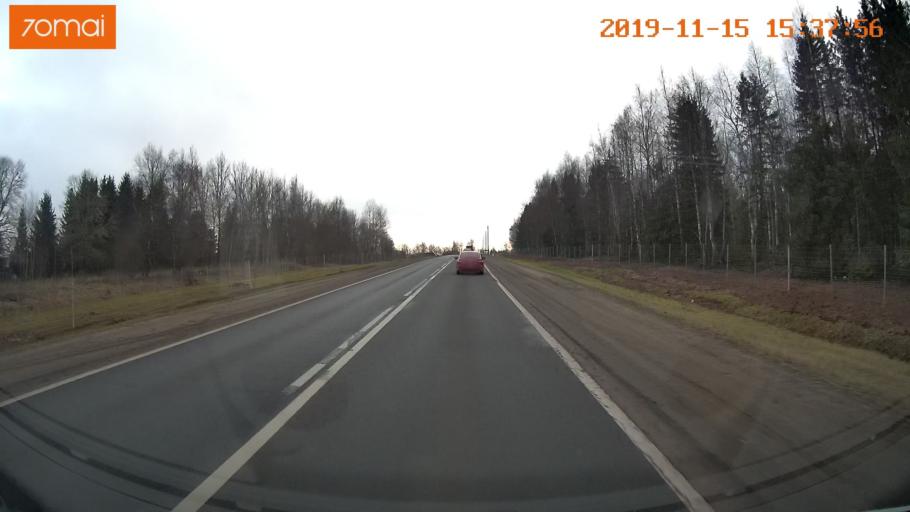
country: RU
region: Jaroslavl
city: Danilov
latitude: 58.0345
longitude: 40.0852
